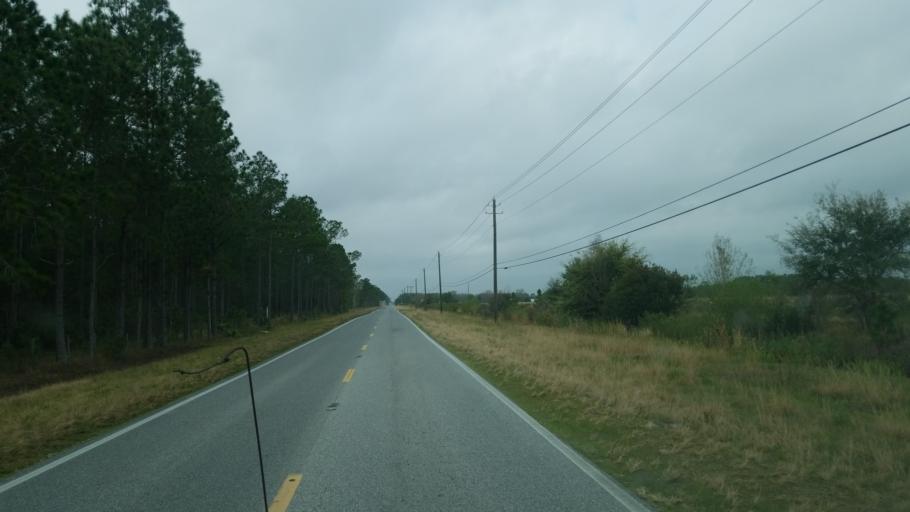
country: US
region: Florida
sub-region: Polk County
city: Polk City
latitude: 28.2591
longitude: -81.8846
